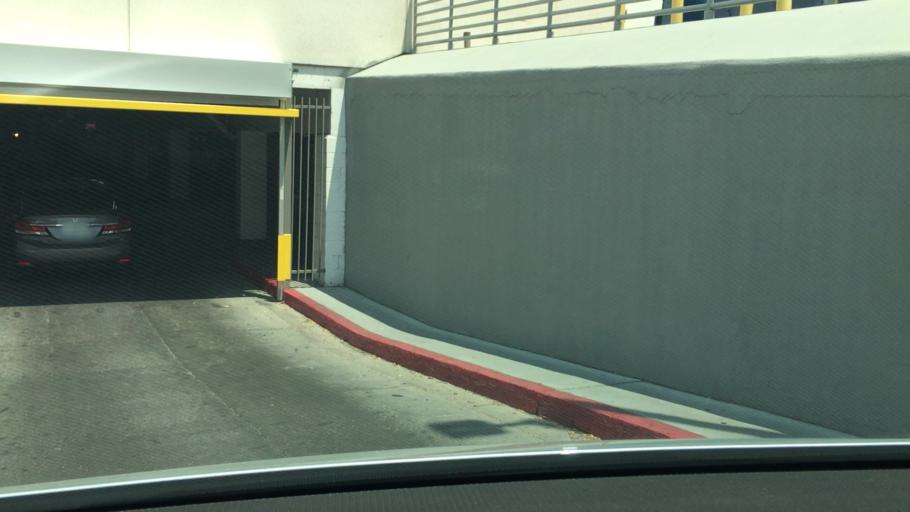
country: US
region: Nevada
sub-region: Clark County
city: Paradise
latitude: 36.1262
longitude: -115.1708
